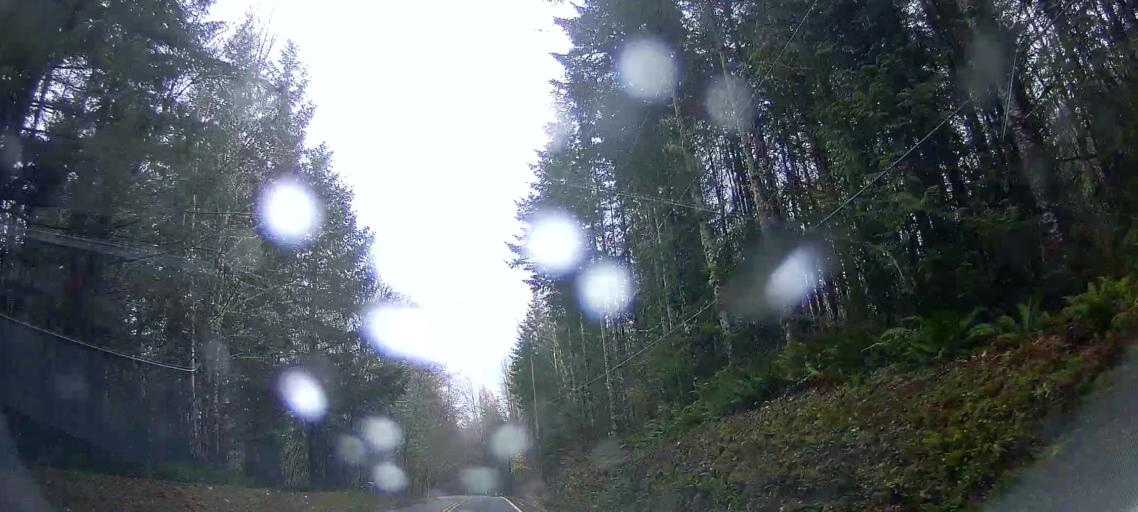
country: US
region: Washington
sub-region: Skagit County
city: Clear Lake
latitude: 48.4767
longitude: -122.1454
